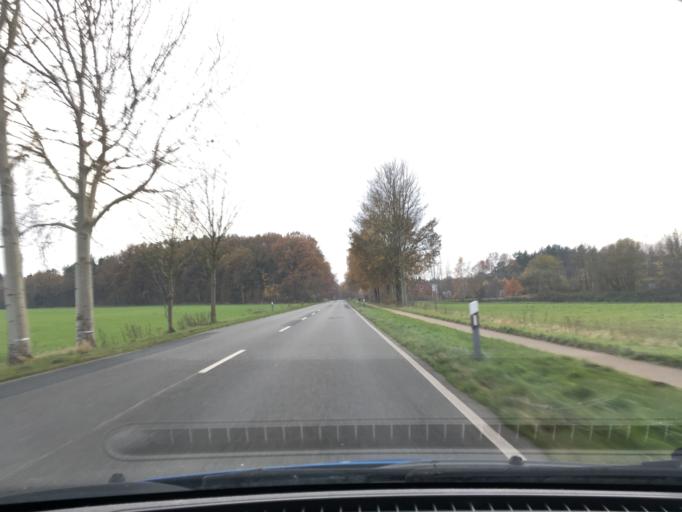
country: DE
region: Lower Saxony
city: Embsen
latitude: 53.2059
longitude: 10.3626
